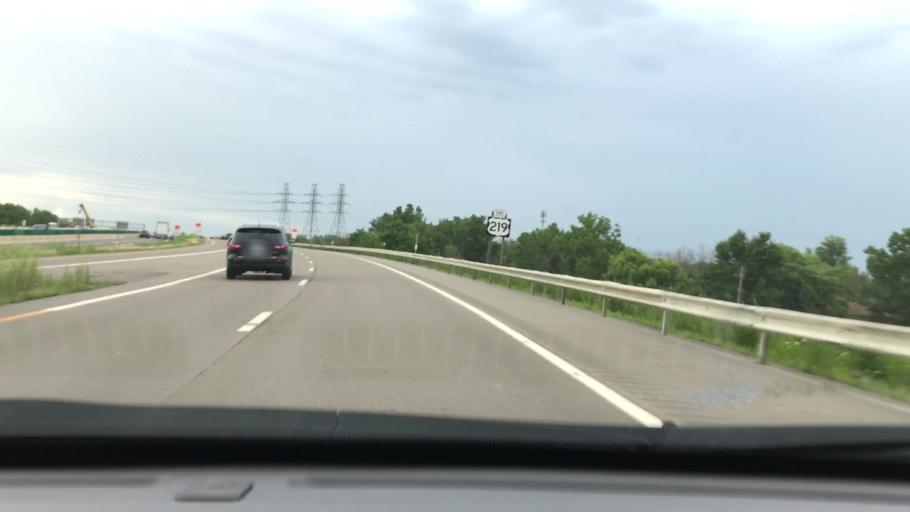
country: US
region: New York
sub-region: Erie County
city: Lackawanna
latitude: 42.8166
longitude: -78.7905
